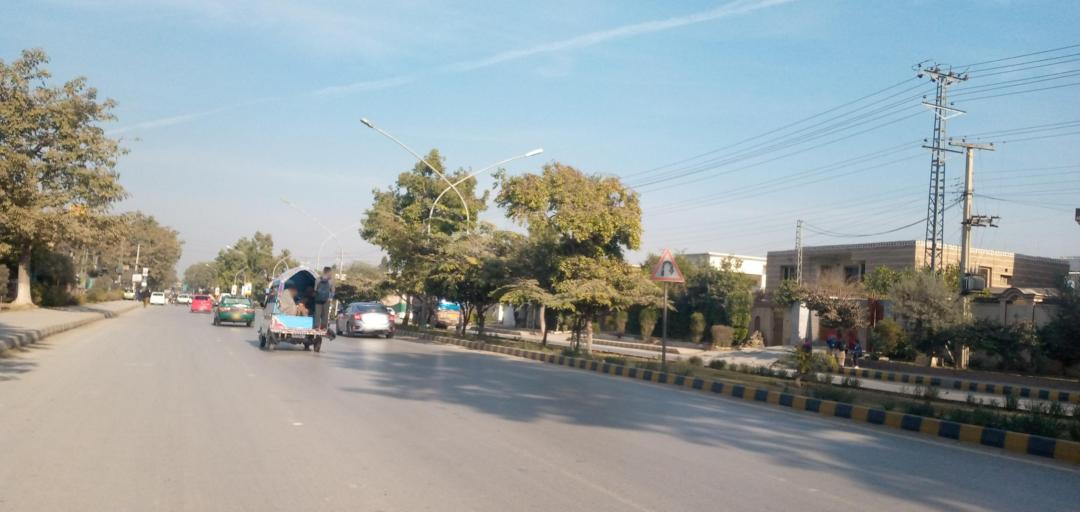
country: PK
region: Khyber Pakhtunkhwa
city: Peshawar
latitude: 33.9729
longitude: 71.4432
